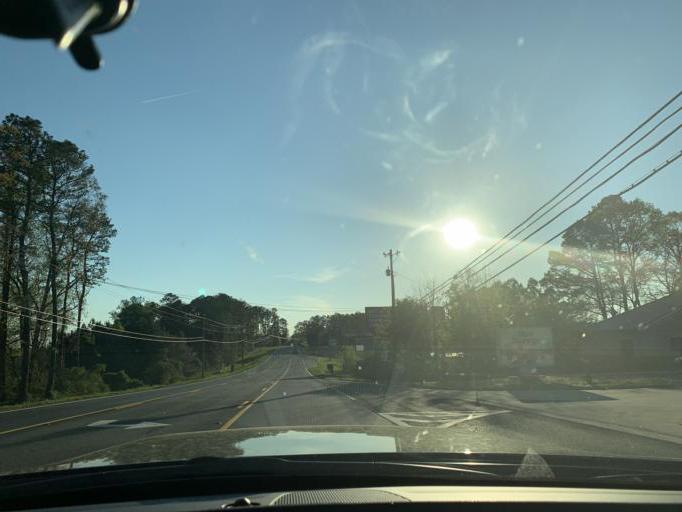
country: US
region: Georgia
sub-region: Forsyth County
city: Cumming
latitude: 34.2381
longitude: -84.2001
